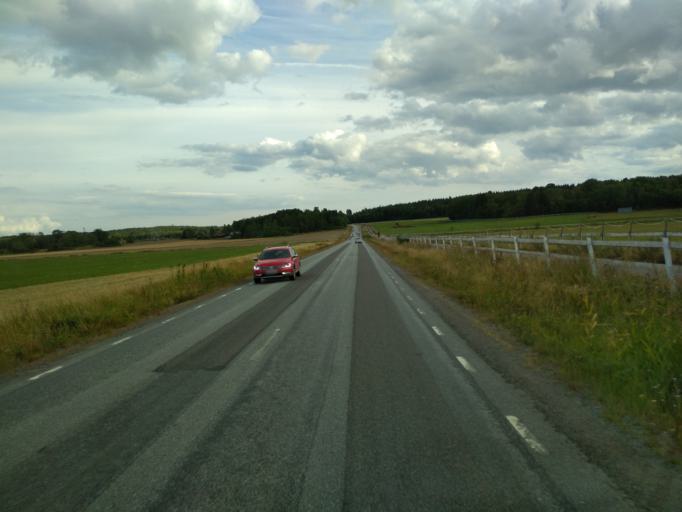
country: SE
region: Uppsala
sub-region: Habo Kommun
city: Balsta
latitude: 59.6619
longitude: 17.5552
